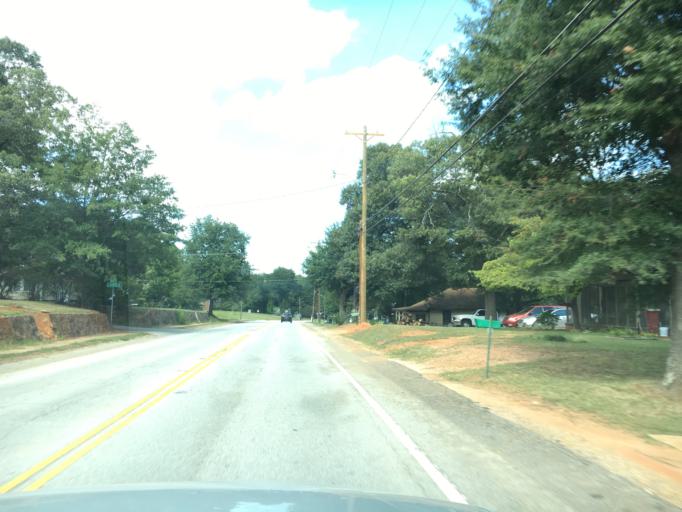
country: US
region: South Carolina
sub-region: Spartanburg County
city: Inman
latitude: 35.0516
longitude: -82.0881
